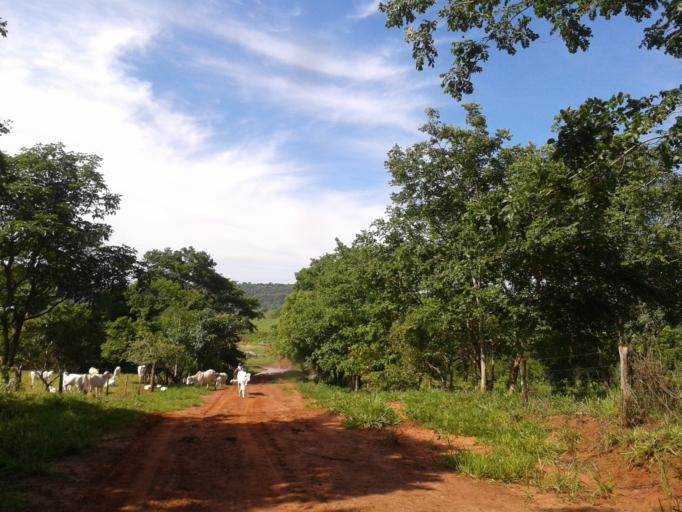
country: BR
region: Minas Gerais
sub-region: Santa Vitoria
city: Santa Vitoria
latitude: -19.0860
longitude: -50.0166
